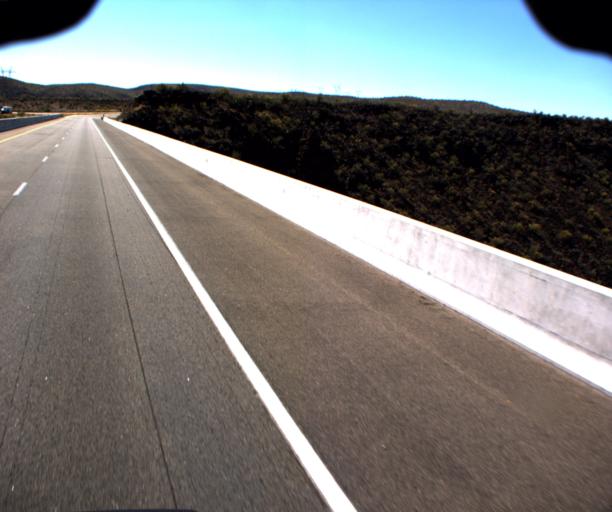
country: US
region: Arizona
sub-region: Yavapai County
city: Bagdad
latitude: 34.5454
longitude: -113.4430
